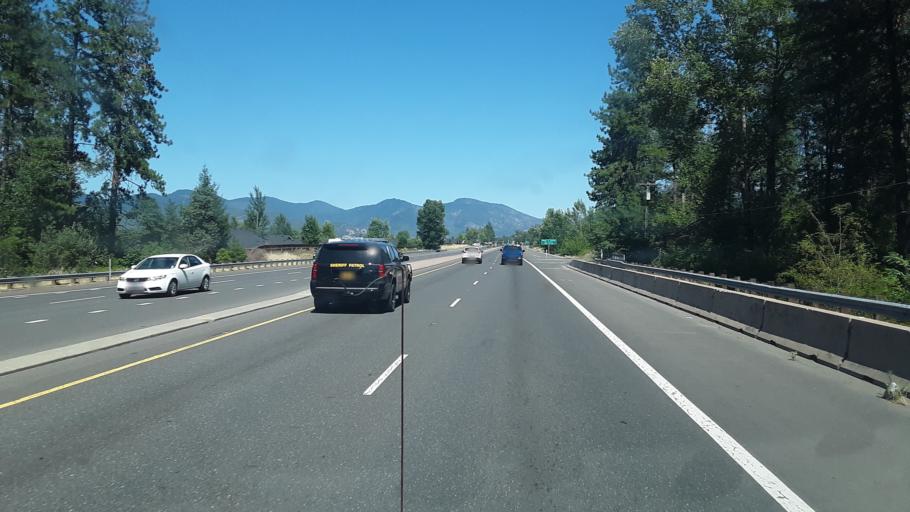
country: US
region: Oregon
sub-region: Josephine County
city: Redwood
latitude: 42.4159
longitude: -123.3850
